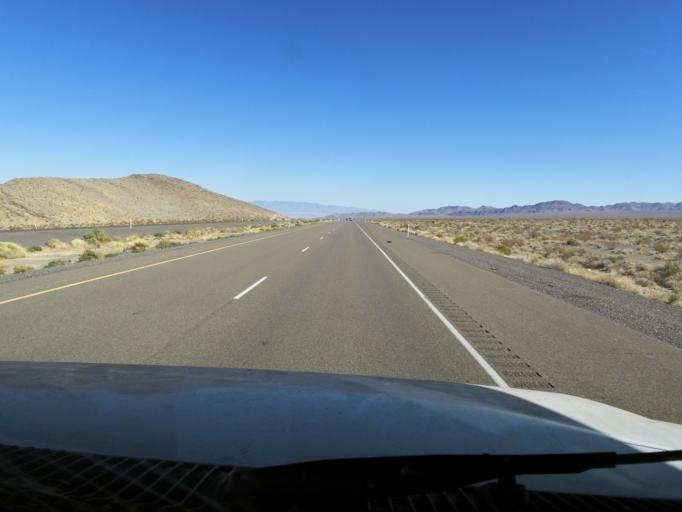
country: US
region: Nevada
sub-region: Nye County
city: Pahrump
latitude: 36.5709
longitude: -115.8612
